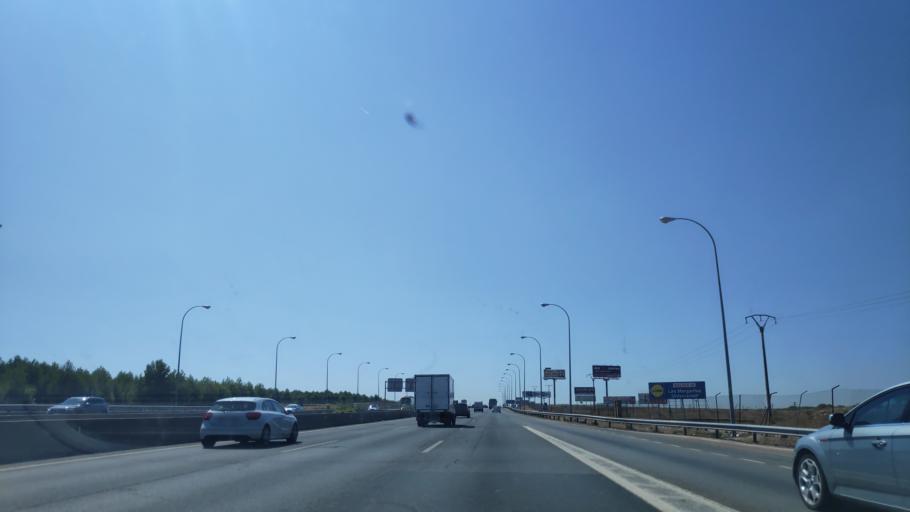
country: ES
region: Madrid
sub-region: Provincia de Madrid
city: Villaverde
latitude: 40.3594
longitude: -3.7216
